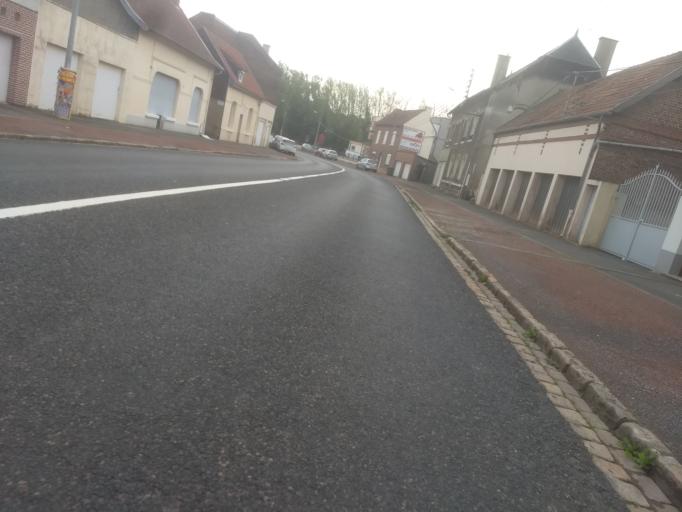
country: FR
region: Nord-Pas-de-Calais
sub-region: Departement du Pas-de-Calais
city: Beaurains
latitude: 50.2642
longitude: 2.7842
